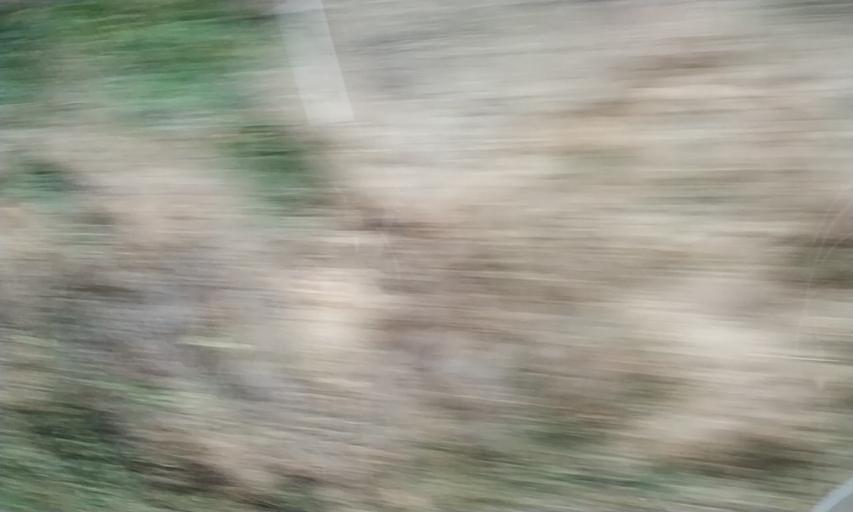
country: PT
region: Vila Real
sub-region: Mesao Frio
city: Mesao Frio
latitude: 41.1804
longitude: -7.8448
